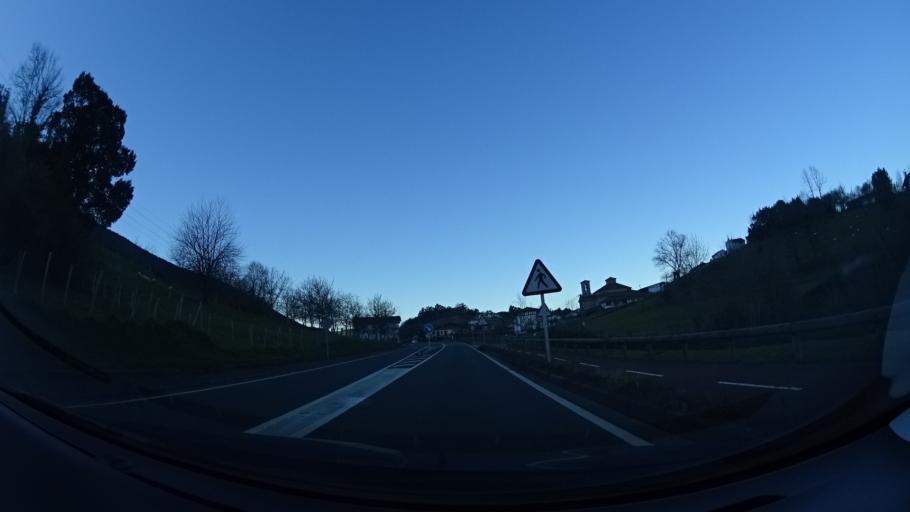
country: ES
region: Basque Country
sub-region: Bizkaia
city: Forua
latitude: 43.3497
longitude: -2.6815
